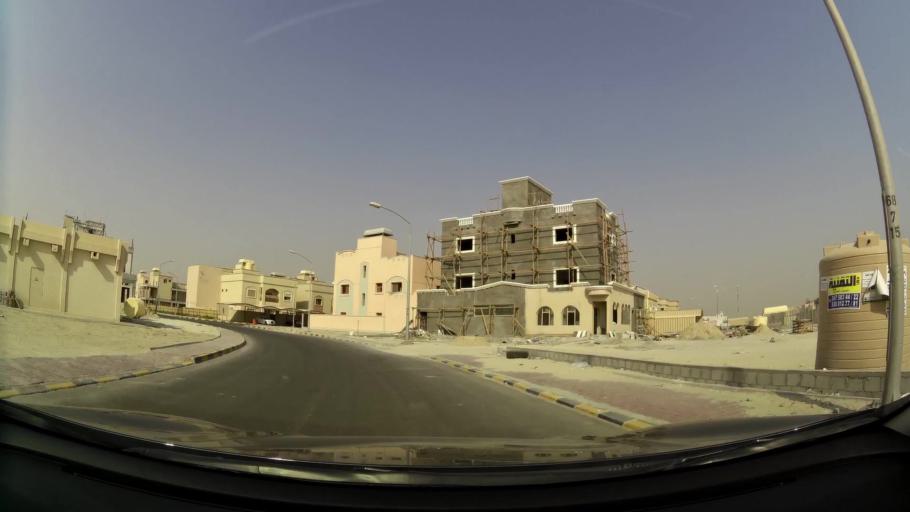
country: KW
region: Muhafazat al Jahra'
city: Al Jahra'
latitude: 29.3532
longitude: 47.7639
